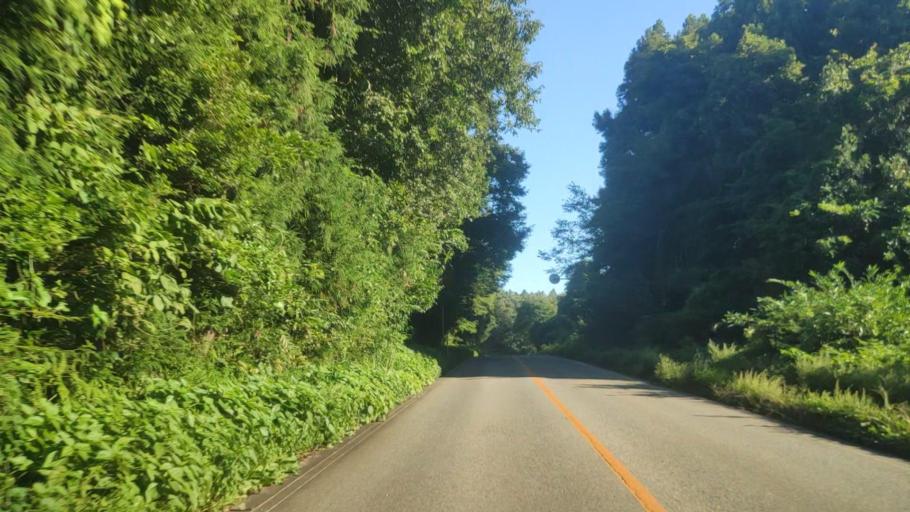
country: JP
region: Ishikawa
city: Nanao
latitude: 37.1036
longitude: 136.9480
